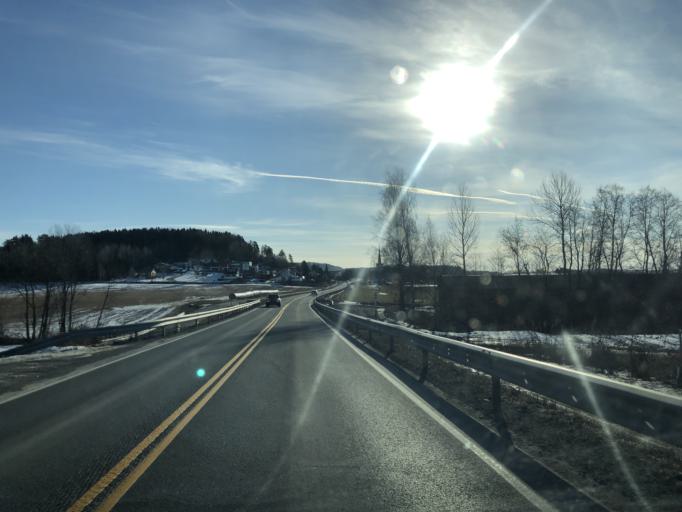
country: NO
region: Hedmark
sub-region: Ringsaker
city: Moelv
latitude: 60.9074
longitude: 10.7100
